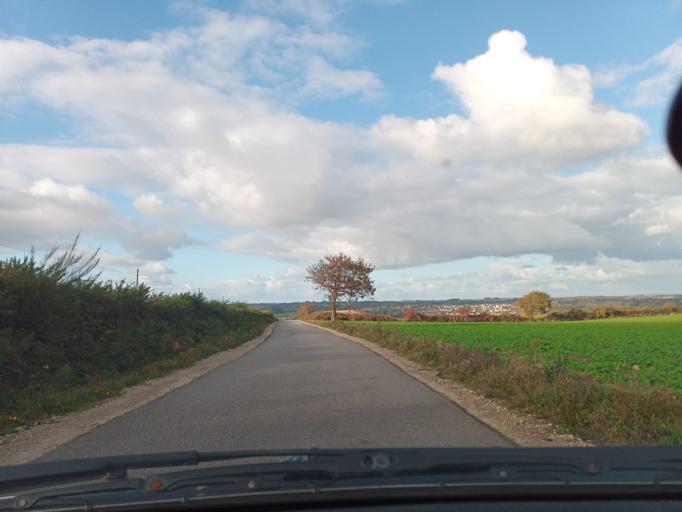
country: FR
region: Brittany
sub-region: Departement du Finistere
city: Plouhinec
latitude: 48.0247
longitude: -4.4981
